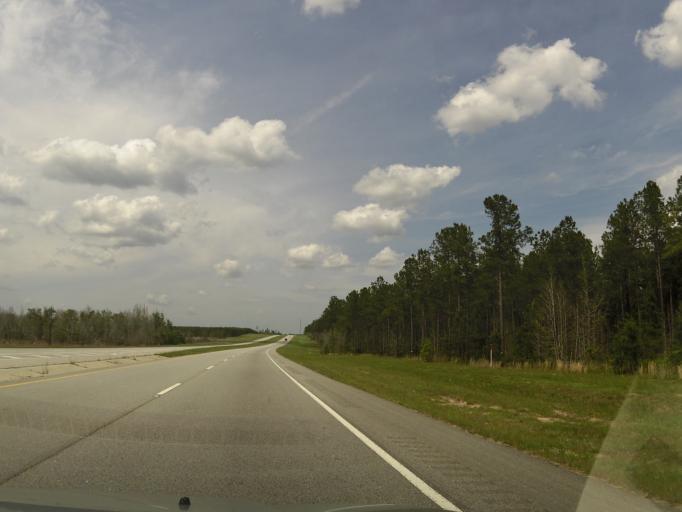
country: US
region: Georgia
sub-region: Jefferson County
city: Wadley
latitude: 32.7264
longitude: -82.3949
